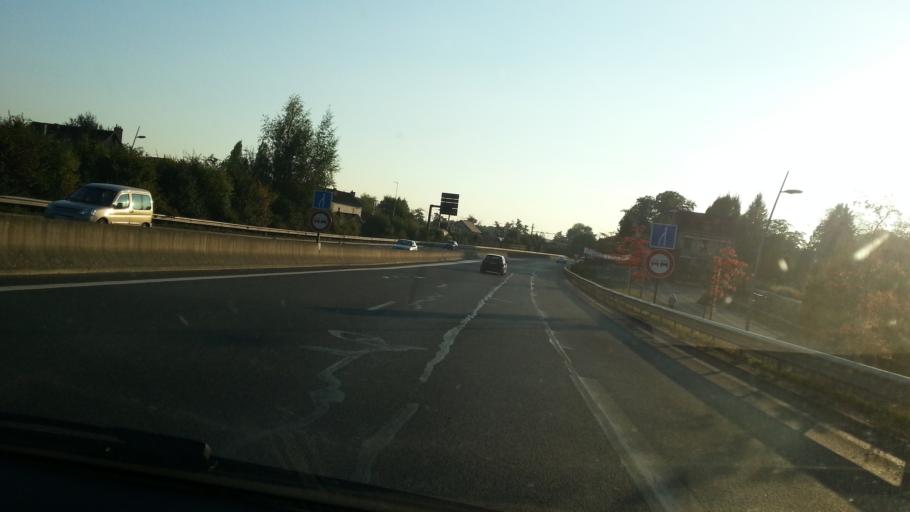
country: FR
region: Picardie
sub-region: Departement de l'Oise
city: Rieux
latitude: 49.2989
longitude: 2.5204
